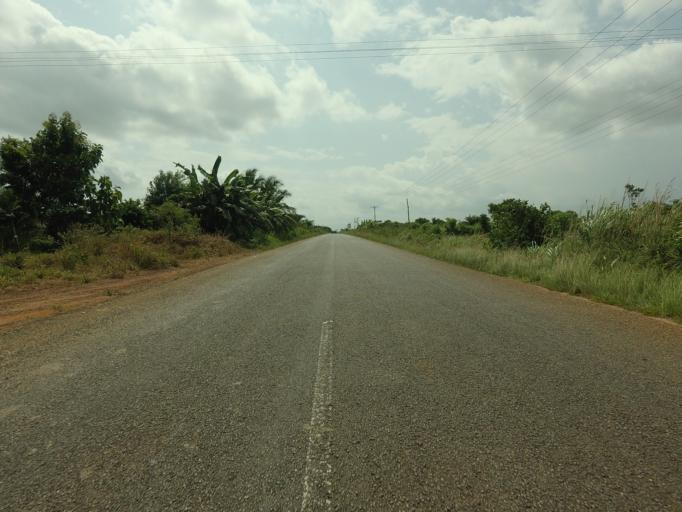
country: TG
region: Maritime
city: Lome
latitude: 6.2111
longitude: 1.0496
